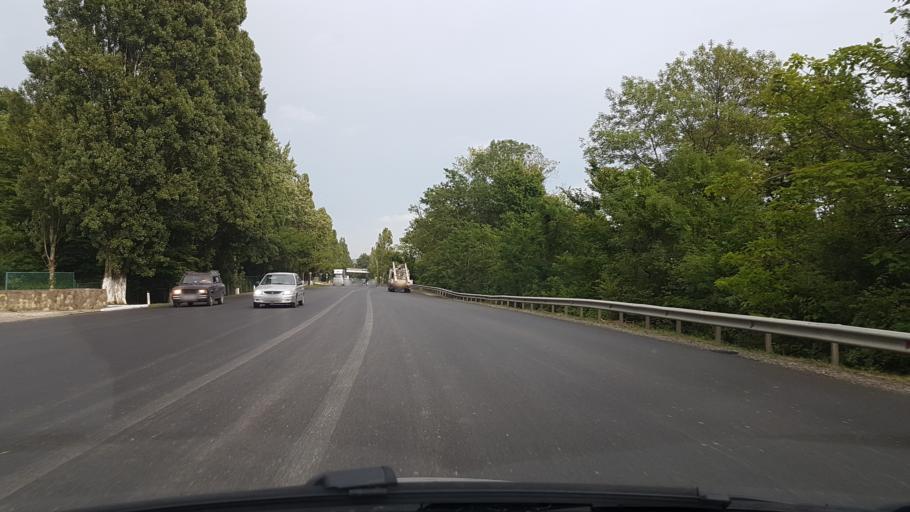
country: RU
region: Krasnodarskiy
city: Lermontovo
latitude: 44.2867
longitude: 38.7803
